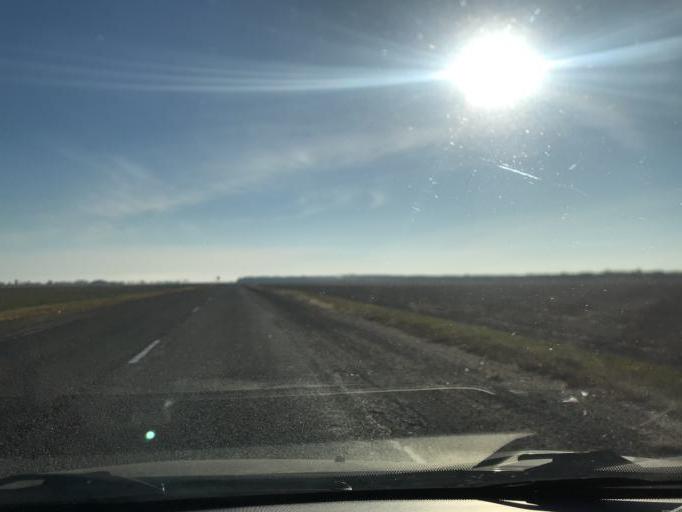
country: BY
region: Gomel
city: Brahin
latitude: 51.7895
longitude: 30.1837
